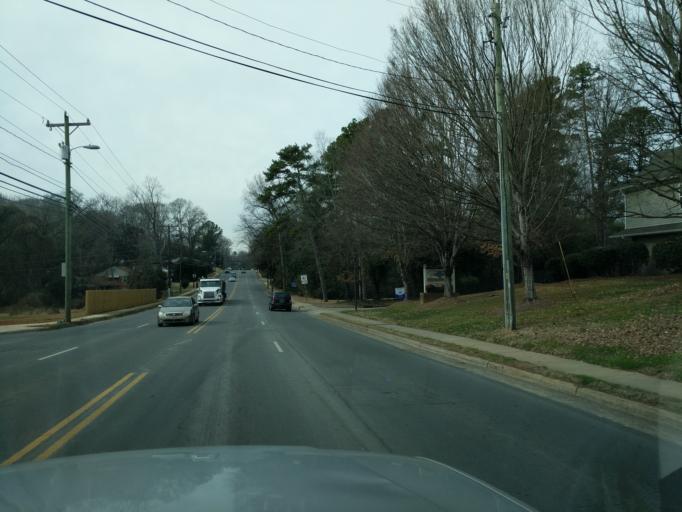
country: US
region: North Carolina
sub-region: Mecklenburg County
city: Charlotte
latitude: 35.1723
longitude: -80.8536
